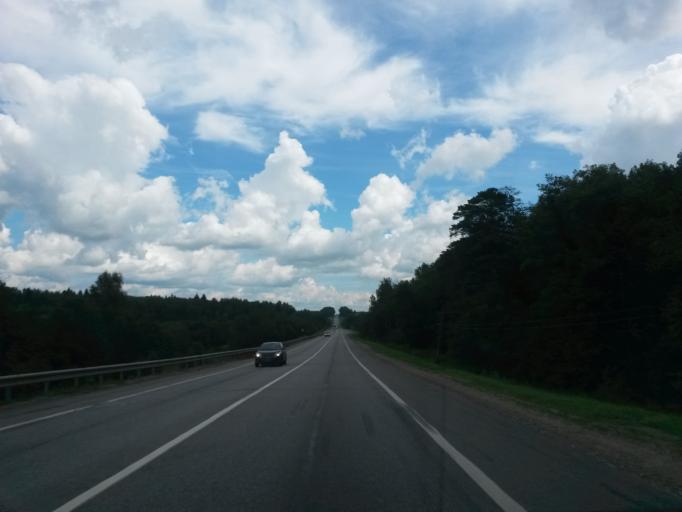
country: RU
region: Vladimir
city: Balakirevo
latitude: 56.6137
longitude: 38.6464
